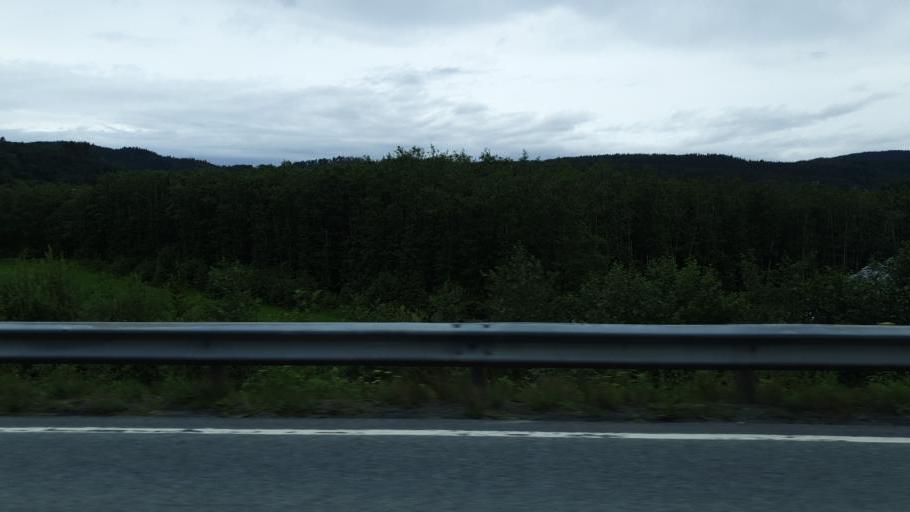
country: NO
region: Sor-Trondelag
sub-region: Melhus
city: Lundamo
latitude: 63.1047
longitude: 10.2356
